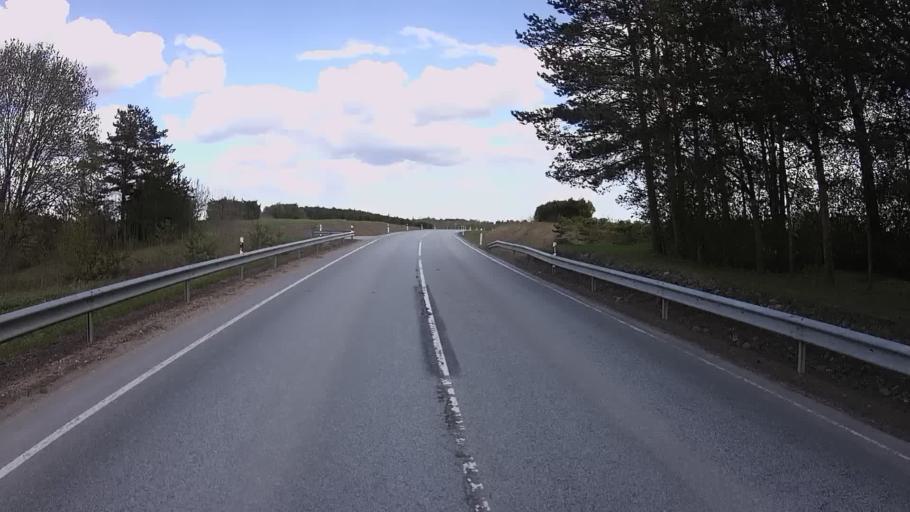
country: EE
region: Jogevamaa
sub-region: Mustvee linn
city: Mustvee
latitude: 58.8267
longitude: 26.6709
